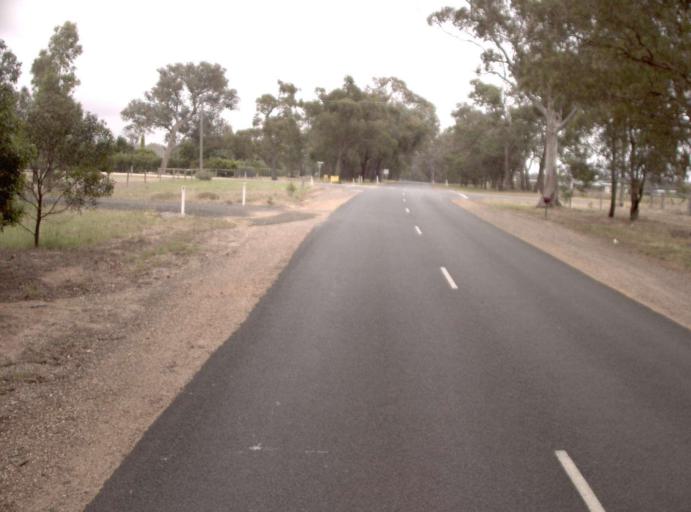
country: AU
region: Victoria
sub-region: Wellington
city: Heyfield
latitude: -37.9712
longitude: 146.7798
